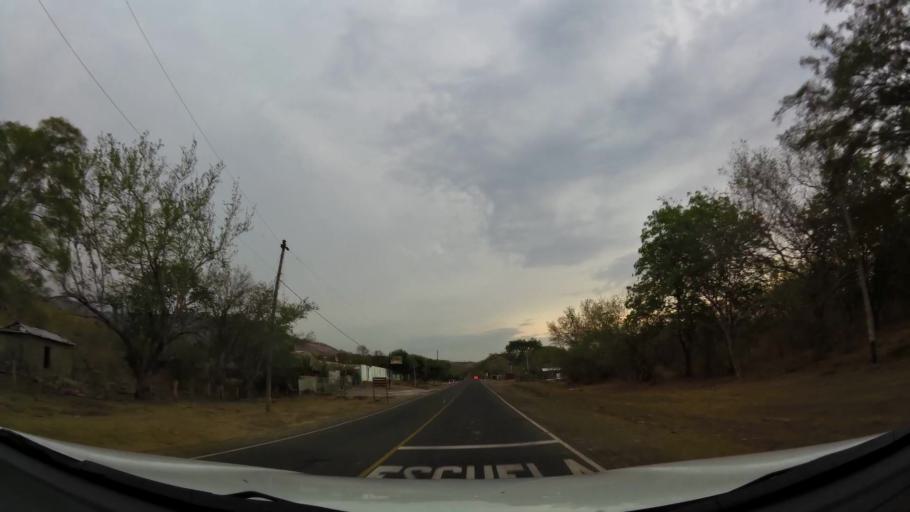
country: NI
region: Leon
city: La Jicaral
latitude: 12.7127
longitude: -86.3948
